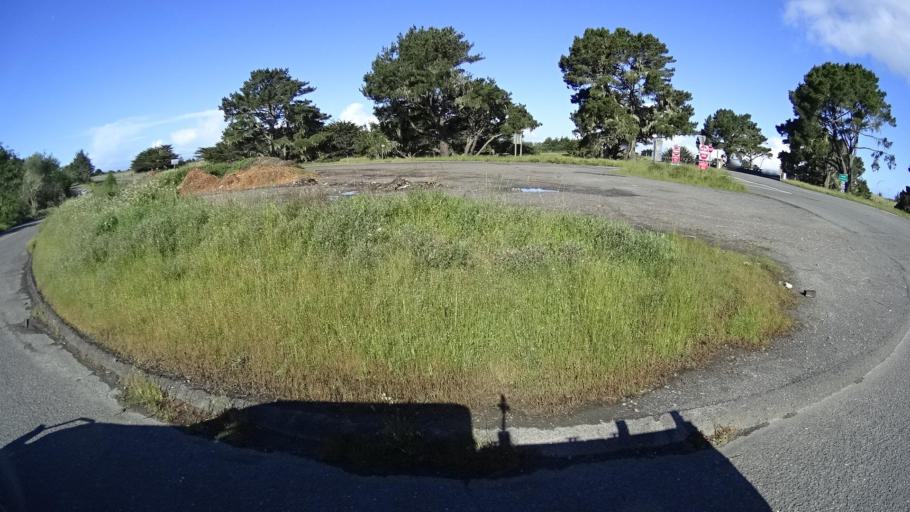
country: US
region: California
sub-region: Humboldt County
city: Westhaven-Moonstone
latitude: 41.0130
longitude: -124.1073
